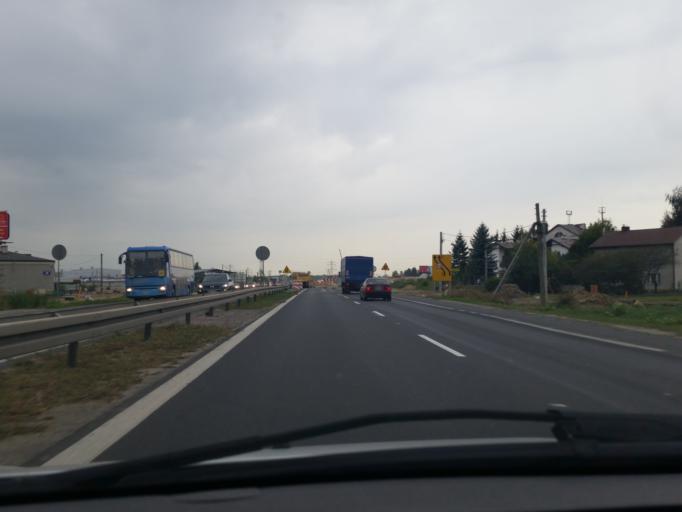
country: PL
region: Masovian Voivodeship
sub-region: Powiat pruszkowski
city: Nowe Grocholice
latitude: 52.1284
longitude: 20.8839
